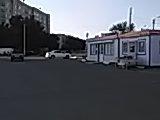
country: RU
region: Orenburg
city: Novotroitsk
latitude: 51.1945
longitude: 58.2965
